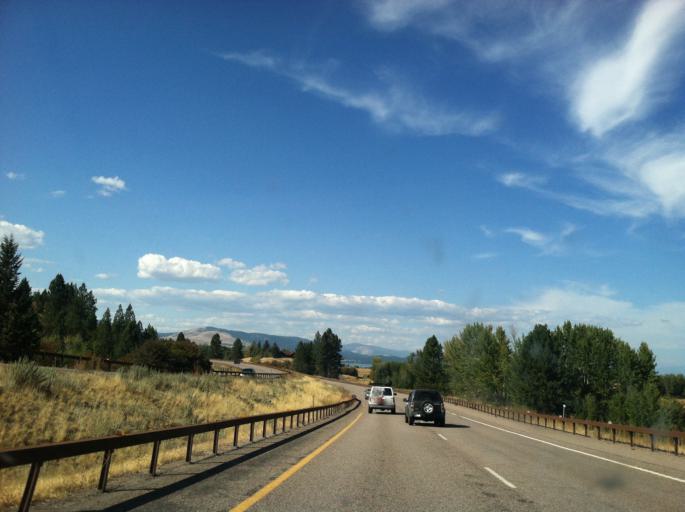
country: US
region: Montana
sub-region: Lake County
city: Polson
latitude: 47.6748
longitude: -114.1071
